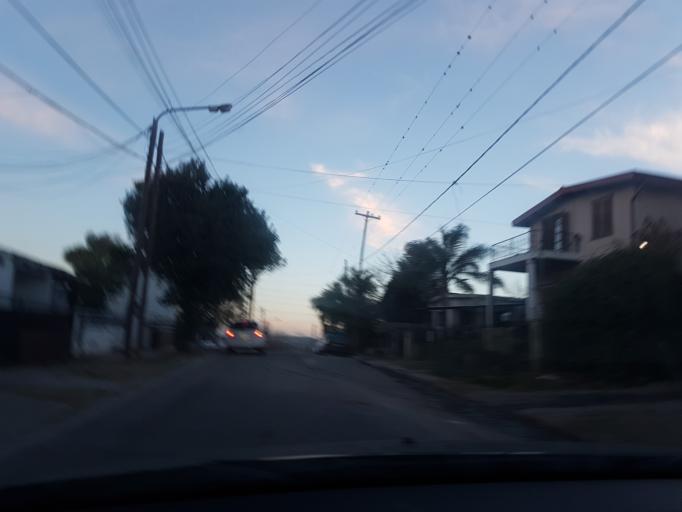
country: AR
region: Cordoba
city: Villa Allende
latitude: -31.2885
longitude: -64.2982
